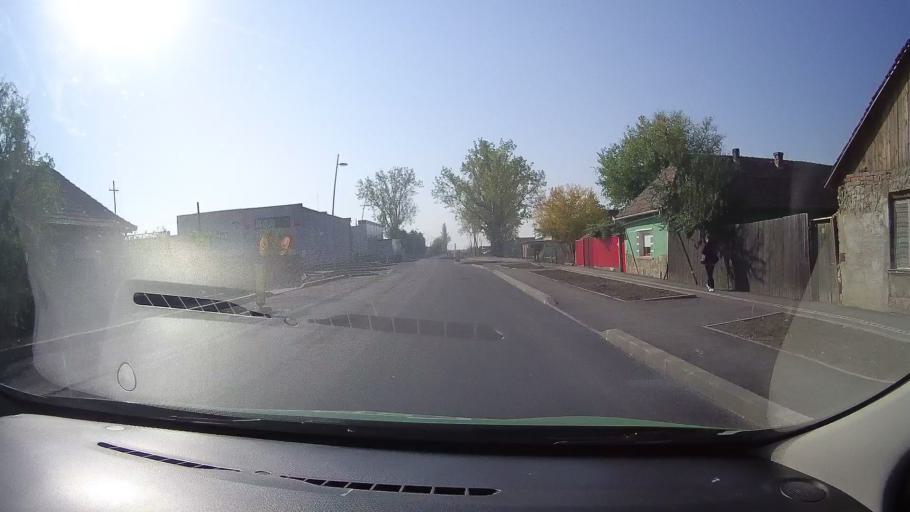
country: RO
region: Bihor
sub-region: Municipiul Salonta
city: Salonta
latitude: 46.7942
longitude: 21.6649
